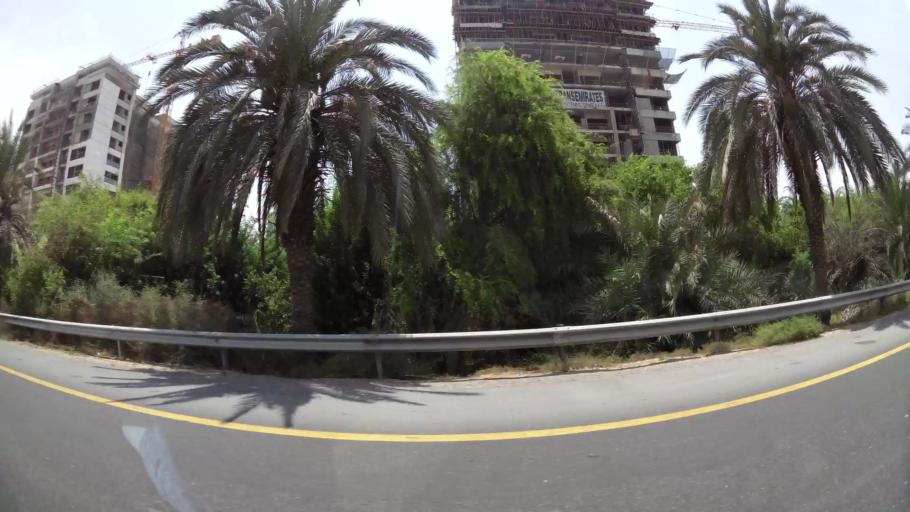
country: AE
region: Ash Shariqah
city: Sharjah
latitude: 25.1909
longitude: 55.3964
